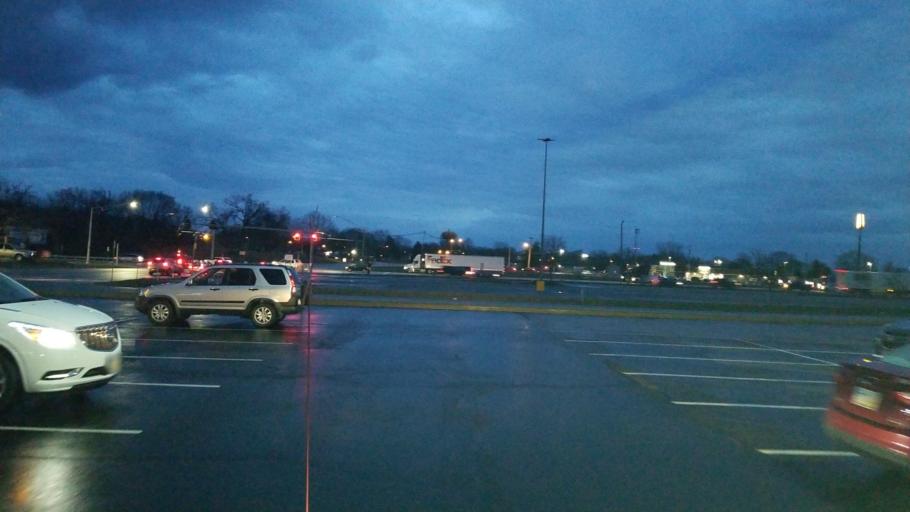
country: US
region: Ohio
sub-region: Pickaway County
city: Circleville
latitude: 39.5874
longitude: -82.9553
